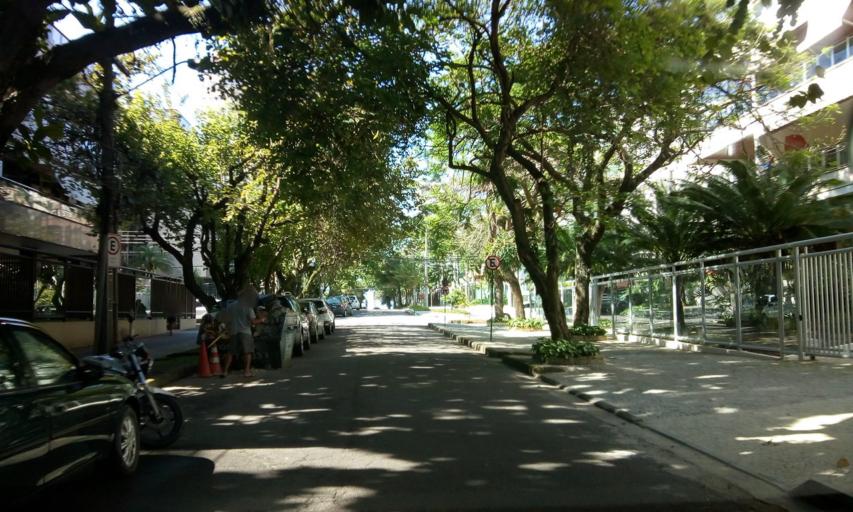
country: BR
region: Rio de Janeiro
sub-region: Rio De Janeiro
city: Rio de Janeiro
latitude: -23.0125
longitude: -43.3095
